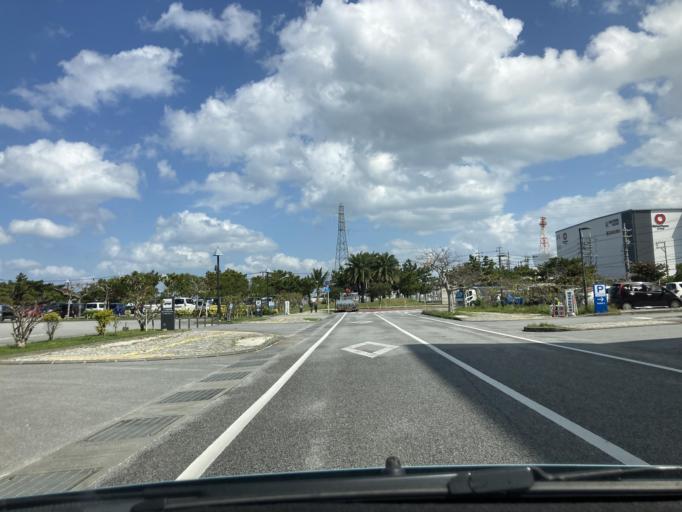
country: JP
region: Okinawa
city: Naha-shi
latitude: 26.2463
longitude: 127.6896
